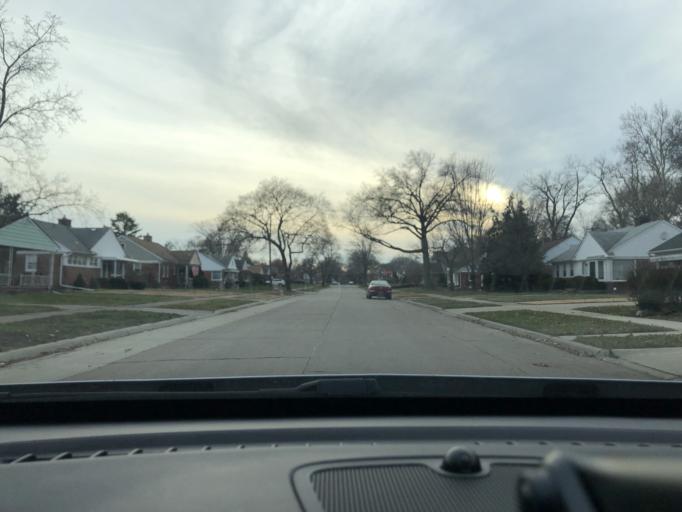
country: US
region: Michigan
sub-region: Wayne County
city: Allen Park
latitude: 42.2913
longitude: -83.2191
